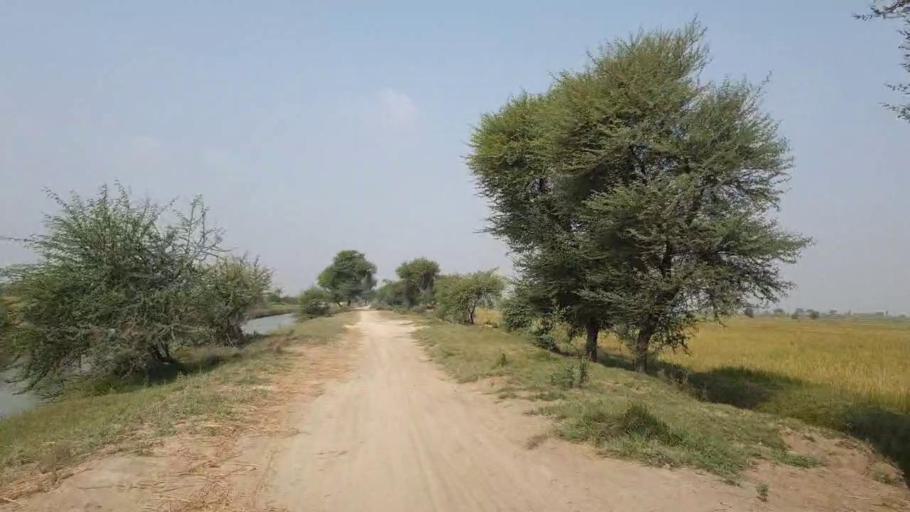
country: PK
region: Sindh
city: Kario
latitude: 24.8390
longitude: 68.5404
